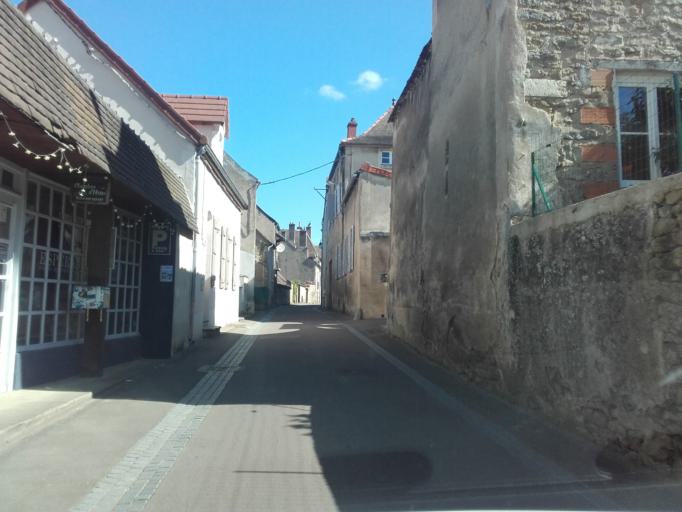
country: FR
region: Bourgogne
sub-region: Departement de la Cote-d'Or
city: Nolay
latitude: 46.9504
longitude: 4.6343
